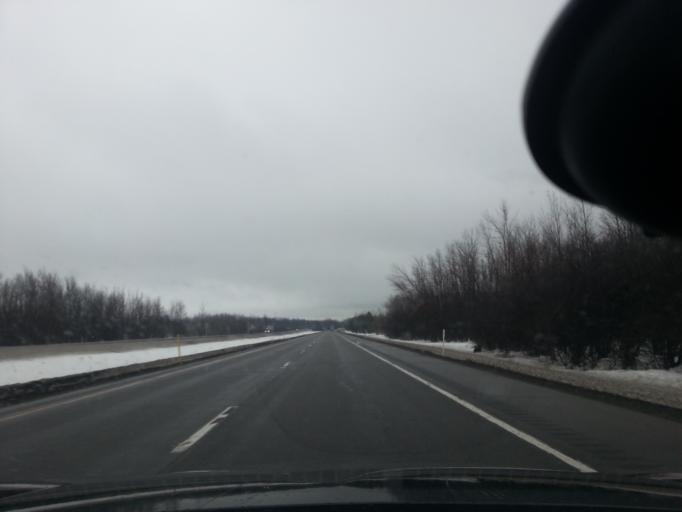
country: US
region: New York
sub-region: Jefferson County
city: Adams Center
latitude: 43.8574
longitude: -76.0181
